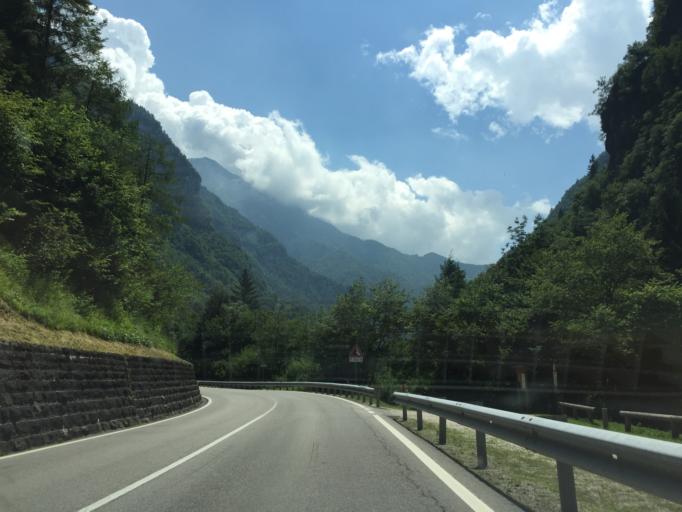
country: IT
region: Trentino-Alto Adige
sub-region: Provincia di Trento
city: Imer
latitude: 46.1239
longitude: 11.7718
